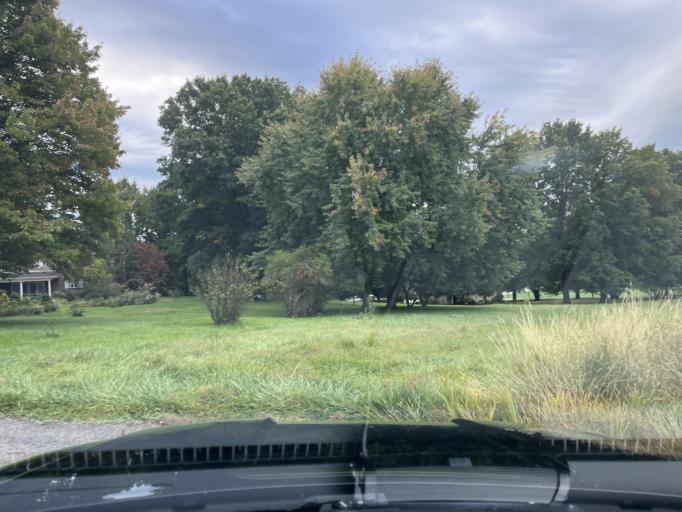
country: US
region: Pennsylvania
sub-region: Fayette County
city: Leith-Hatfield
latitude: 39.8750
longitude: -79.7252
